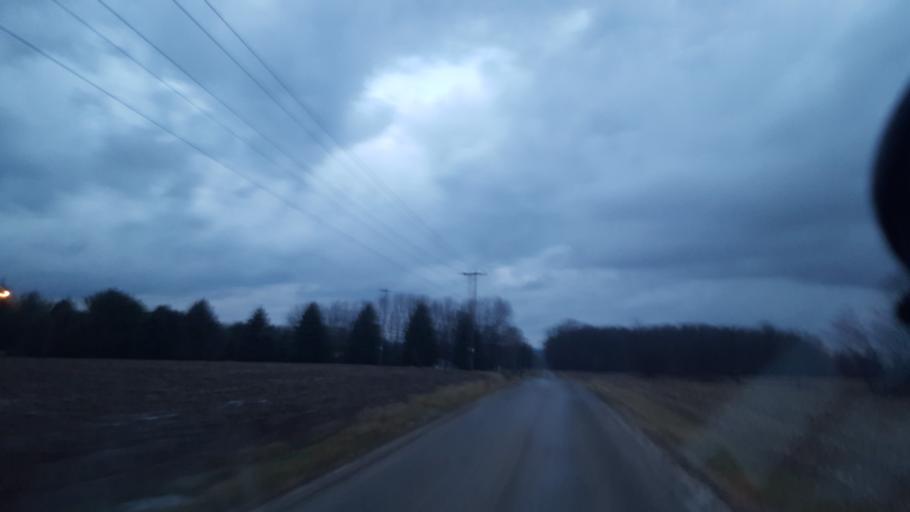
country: US
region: Ohio
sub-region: Richland County
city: Lexington
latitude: 40.6075
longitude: -82.6055
